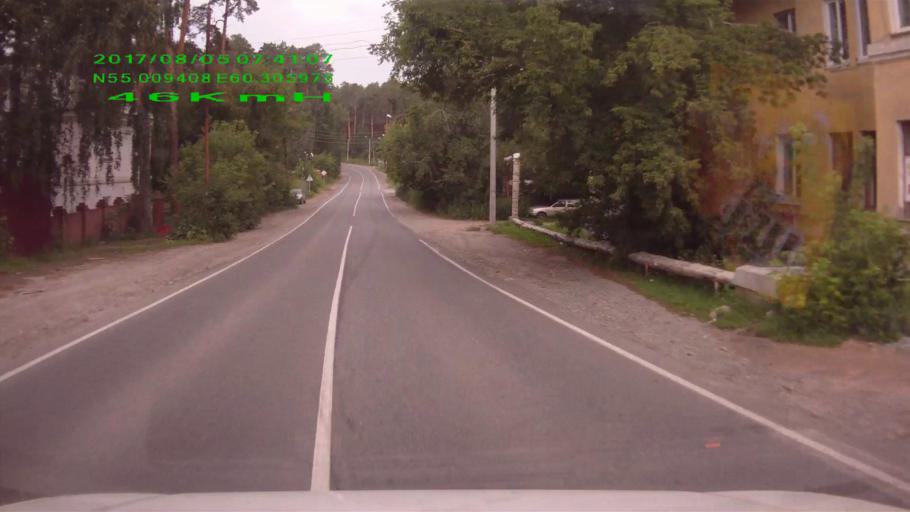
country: RU
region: Chelyabinsk
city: Chebarkul'
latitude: 55.0095
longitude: 60.3058
